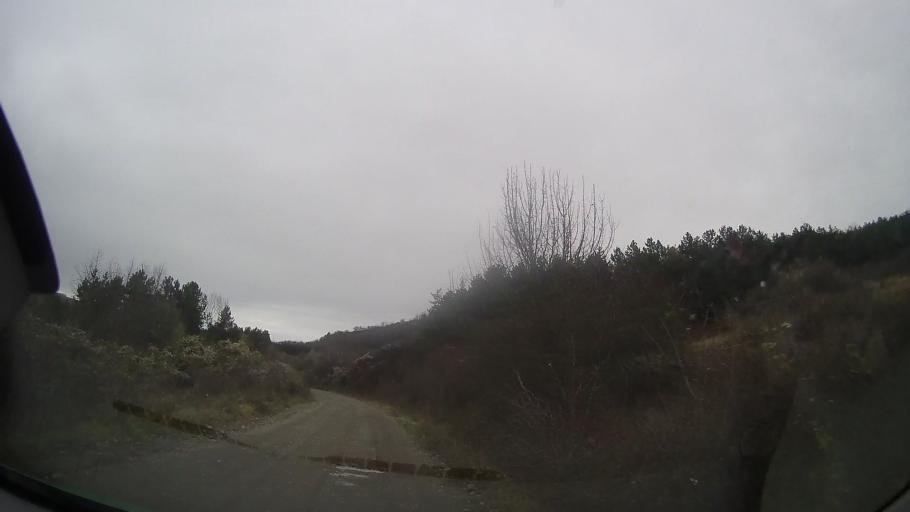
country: RO
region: Mures
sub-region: Comuna Bala
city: Bala
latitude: 46.6798
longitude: 24.4866
